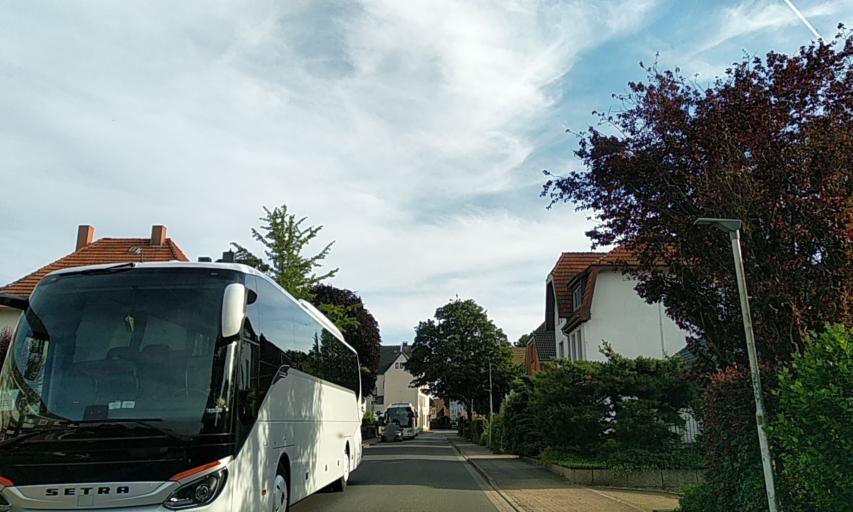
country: DE
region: Schleswig-Holstein
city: Schleswig
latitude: 54.5227
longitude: 9.5575
